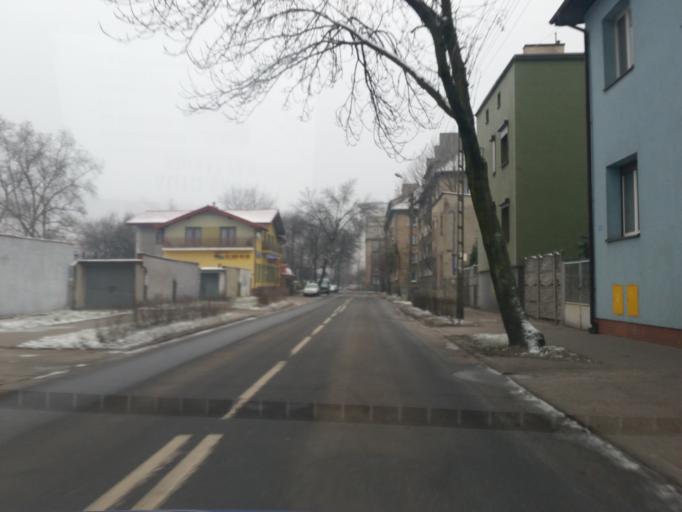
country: PL
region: Silesian Voivodeship
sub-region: Sosnowiec
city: Sosnowiec
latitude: 50.2716
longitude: 19.1207
